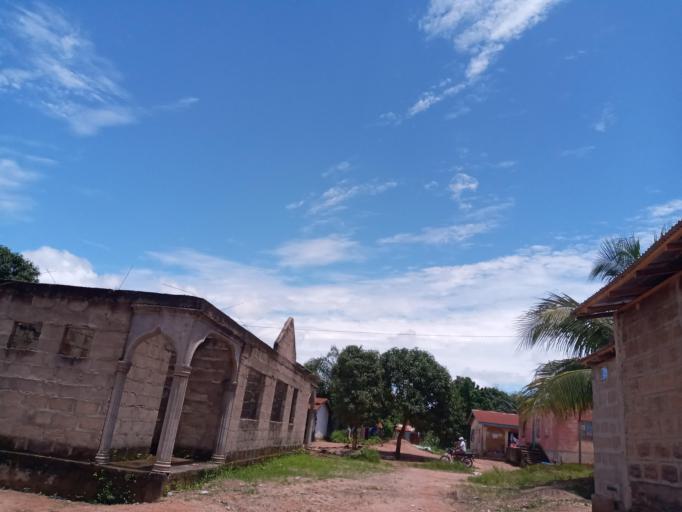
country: SL
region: Eastern Province
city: Koidu
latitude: 8.6490
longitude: -10.9603
